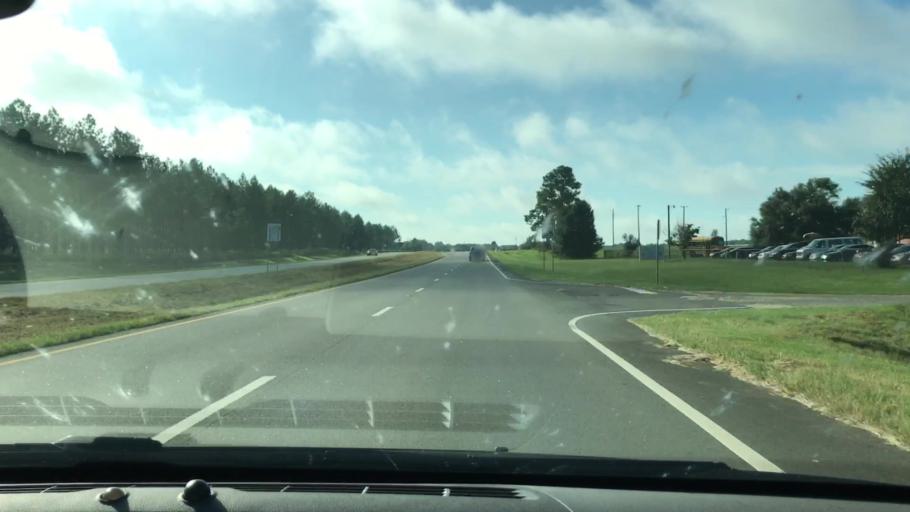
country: US
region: Georgia
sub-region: Terrell County
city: Dawson
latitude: 31.7497
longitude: -84.4208
